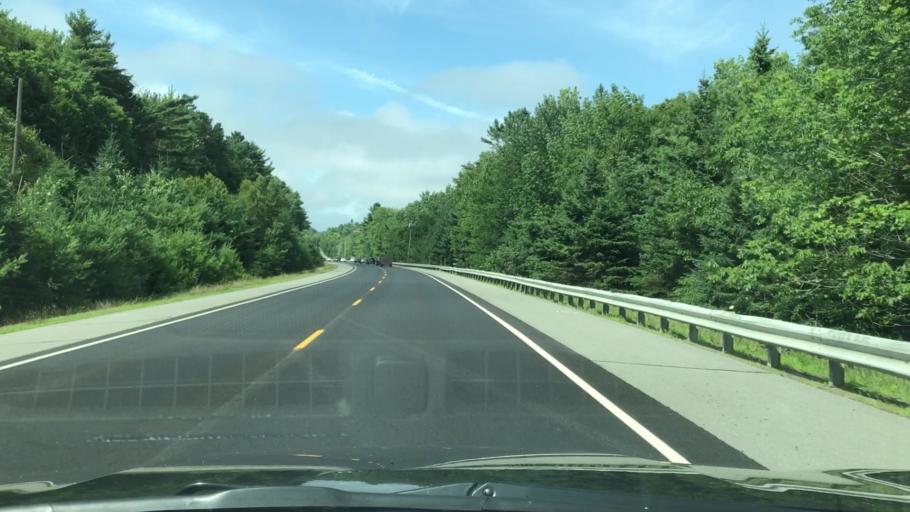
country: US
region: Maine
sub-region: Hancock County
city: Bucksport
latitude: 44.5325
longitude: -68.8085
